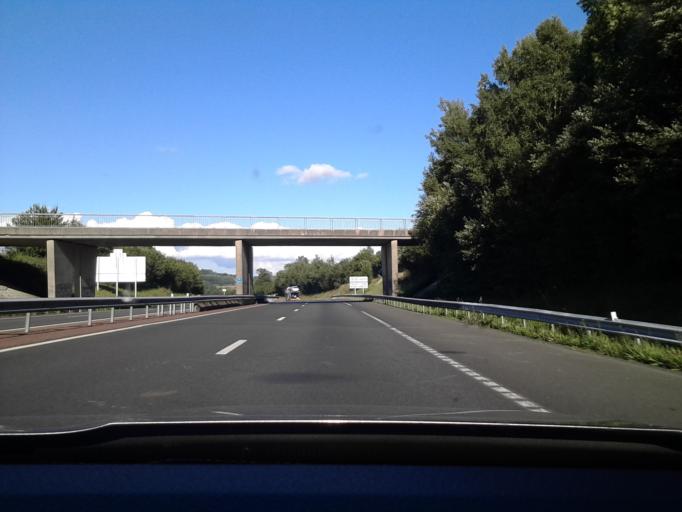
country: FR
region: Lower Normandy
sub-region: Departement de la Manche
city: Tessy-sur-Vire
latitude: 48.9411
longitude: -1.0509
